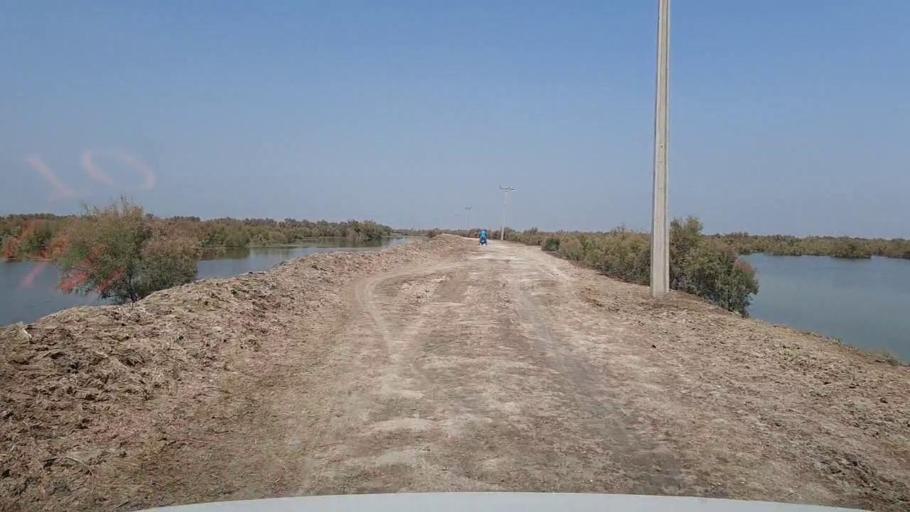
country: PK
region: Sindh
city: Kandhkot
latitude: 28.3470
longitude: 69.3015
